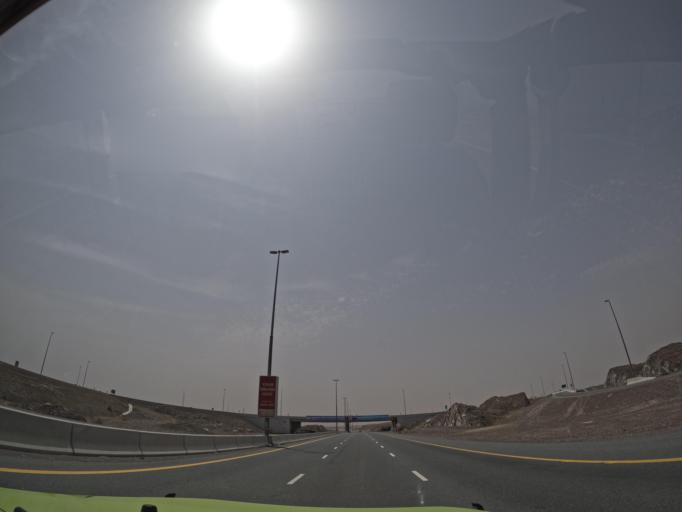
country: AE
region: Ash Shariqah
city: Adh Dhayd
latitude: 25.1586
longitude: 56.0256
